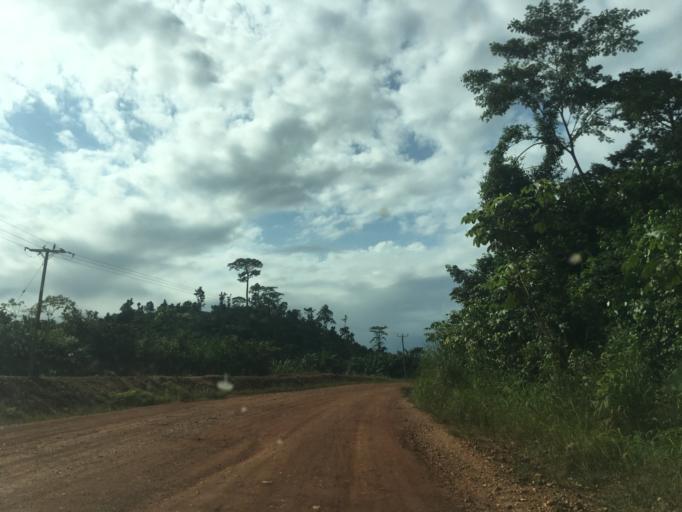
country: GH
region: Western
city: Wassa-Akropong
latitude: 5.9193
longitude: -2.4068
